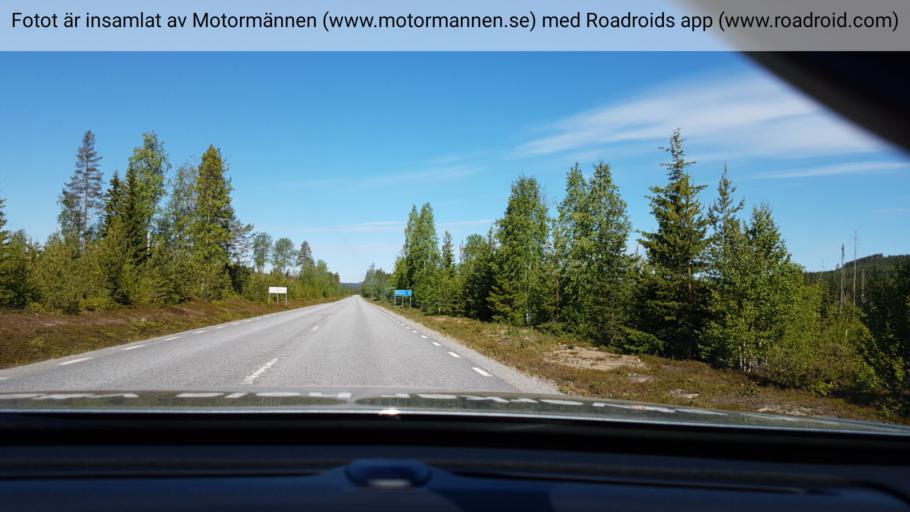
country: SE
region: Vaesterbotten
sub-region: Bjurholms Kommun
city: Bjurholm
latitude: 63.9545
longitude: 18.8813
